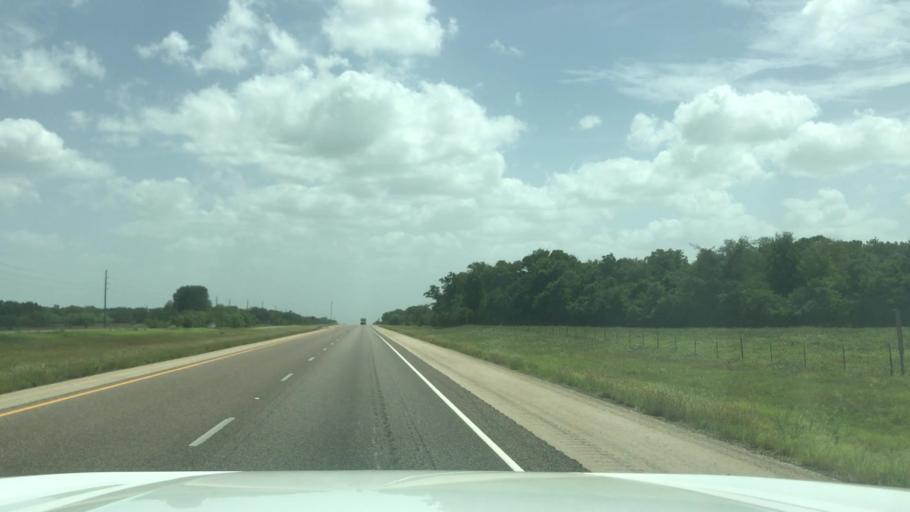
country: US
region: Texas
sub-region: Robertson County
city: Calvert
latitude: 31.0510
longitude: -96.7112
